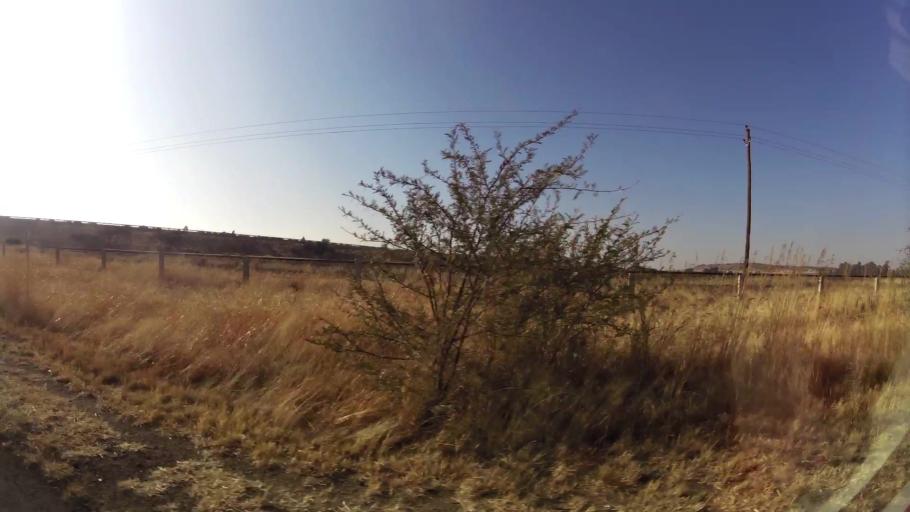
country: ZA
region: Orange Free State
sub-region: Mangaung Metropolitan Municipality
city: Bloemfontein
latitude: -29.1822
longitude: 26.1886
